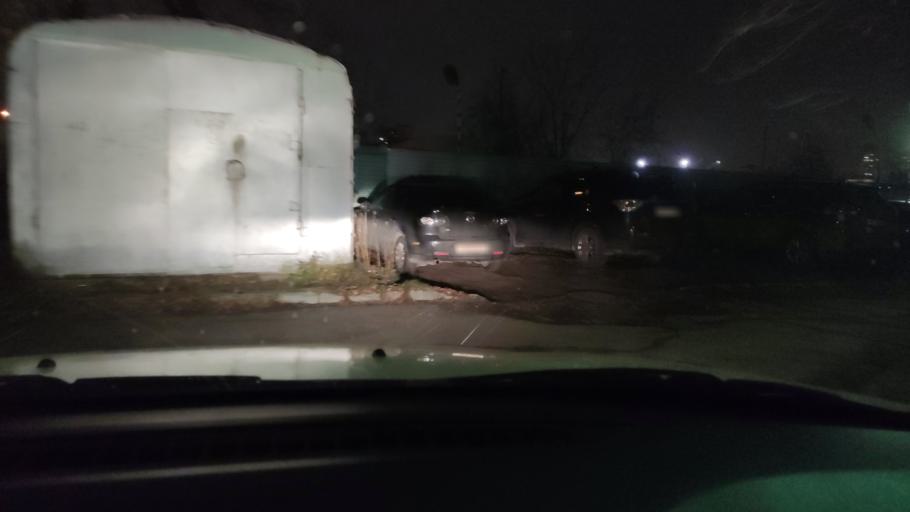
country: RU
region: Perm
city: Perm
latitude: 58.0000
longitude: 56.2034
